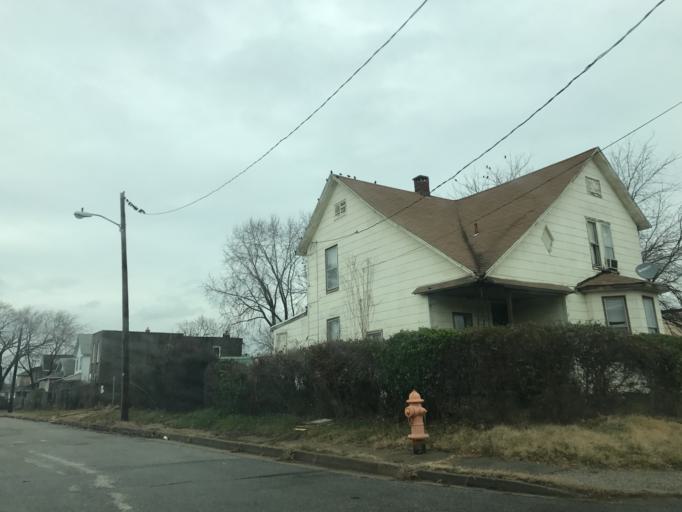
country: US
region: Maryland
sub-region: Baltimore County
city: Rosedale
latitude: 39.3018
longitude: -76.5596
